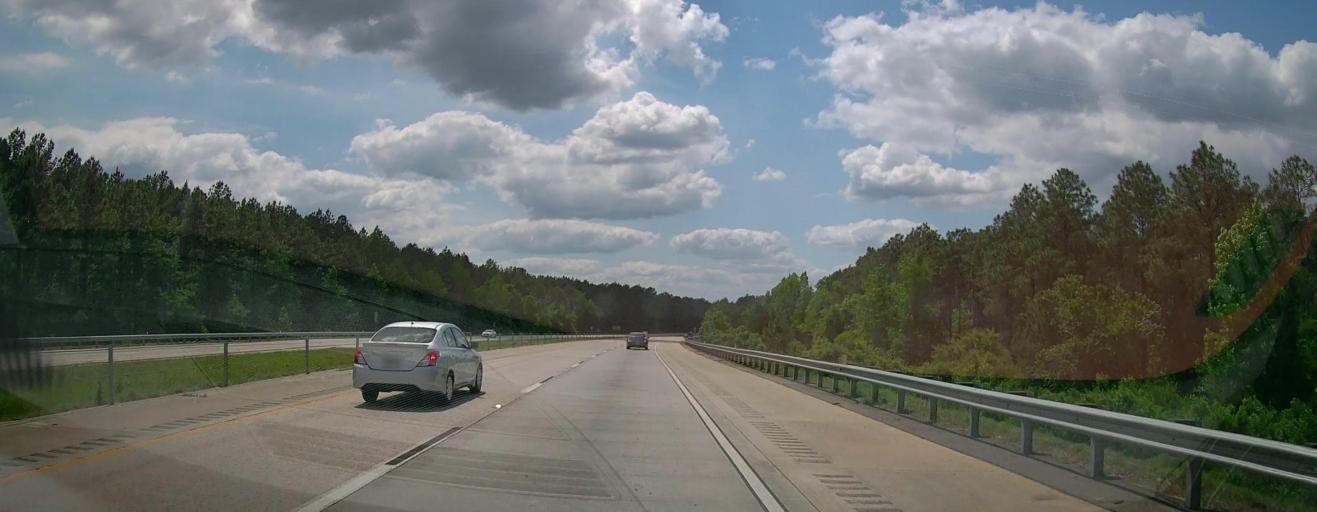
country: US
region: Georgia
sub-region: Treutlen County
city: Soperton
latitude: 32.4353
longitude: -82.6880
